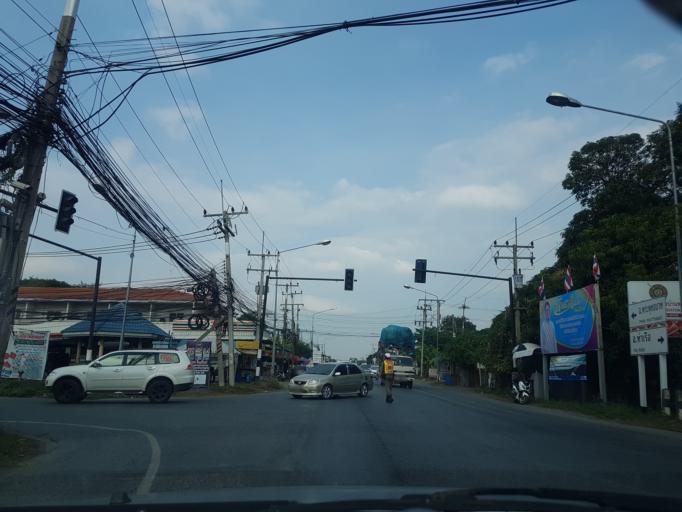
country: TH
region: Sara Buri
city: Ban Mo
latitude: 14.6066
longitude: 100.7379
